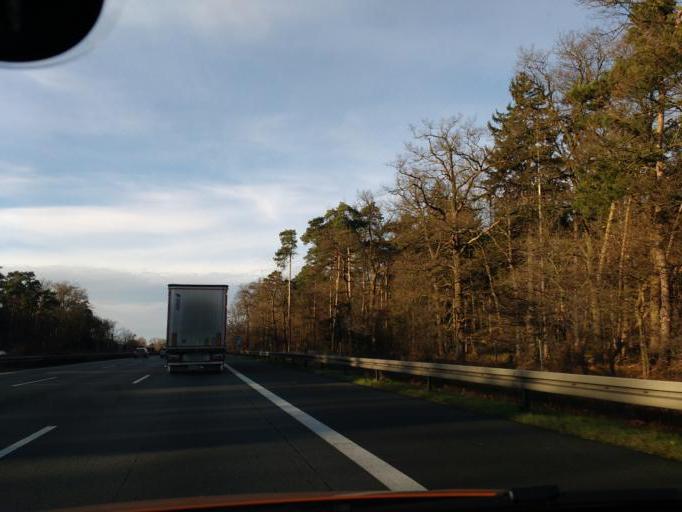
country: DE
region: Lower Saxony
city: Lehrte
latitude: 52.3858
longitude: 10.0068
